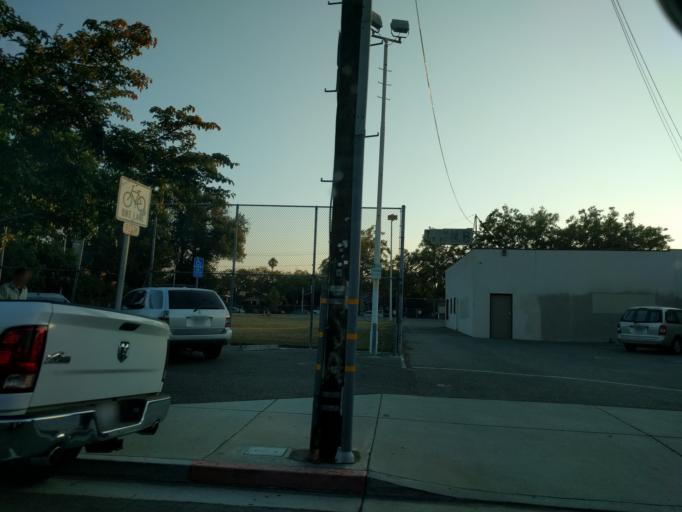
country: US
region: California
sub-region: Santa Clara County
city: San Jose
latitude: 37.3480
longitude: -121.8952
